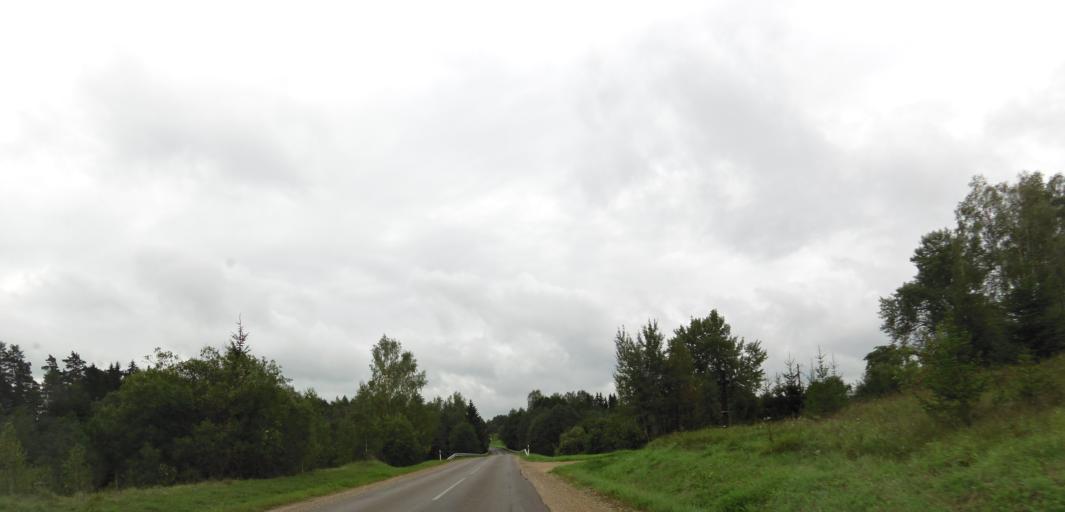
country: LT
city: Moletai
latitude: 55.3278
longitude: 25.3156
